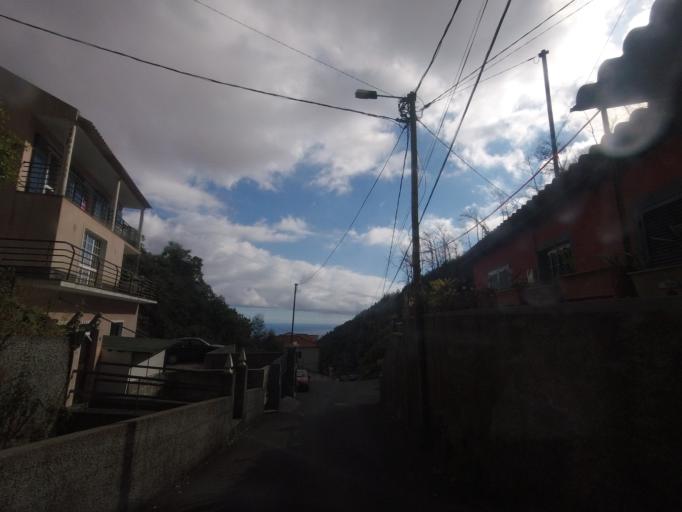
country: PT
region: Madeira
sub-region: Funchal
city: Nossa Senhora do Monte
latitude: 32.6781
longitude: -16.9315
